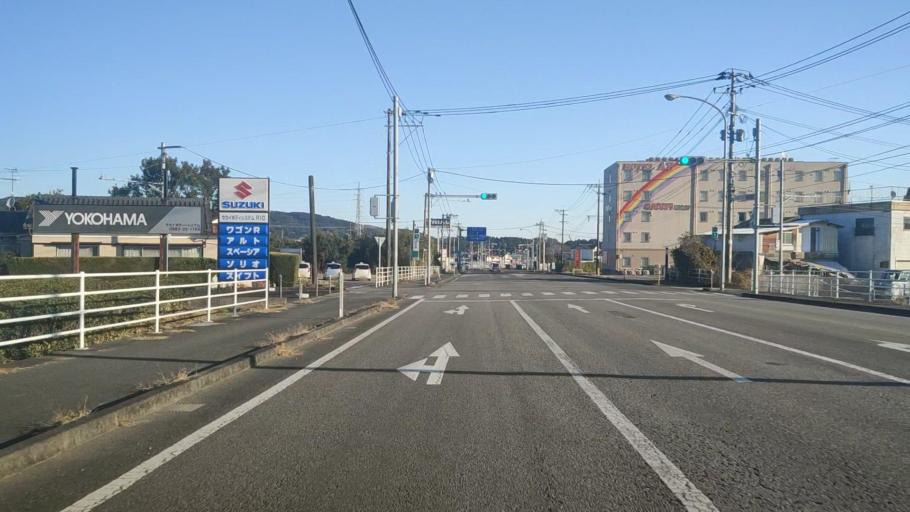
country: JP
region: Miyazaki
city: Takanabe
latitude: 32.2526
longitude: 131.5528
